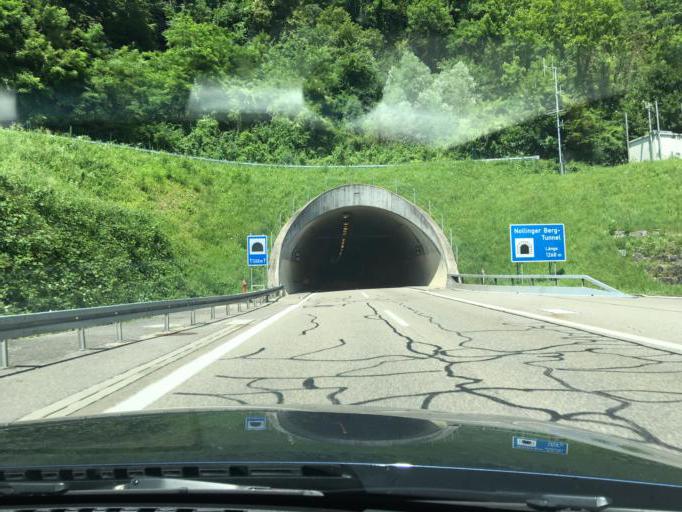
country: DE
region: Baden-Wuerttemberg
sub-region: Freiburg Region
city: Rheinfelden (Baden)
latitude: 47.5712
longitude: 7.7612
